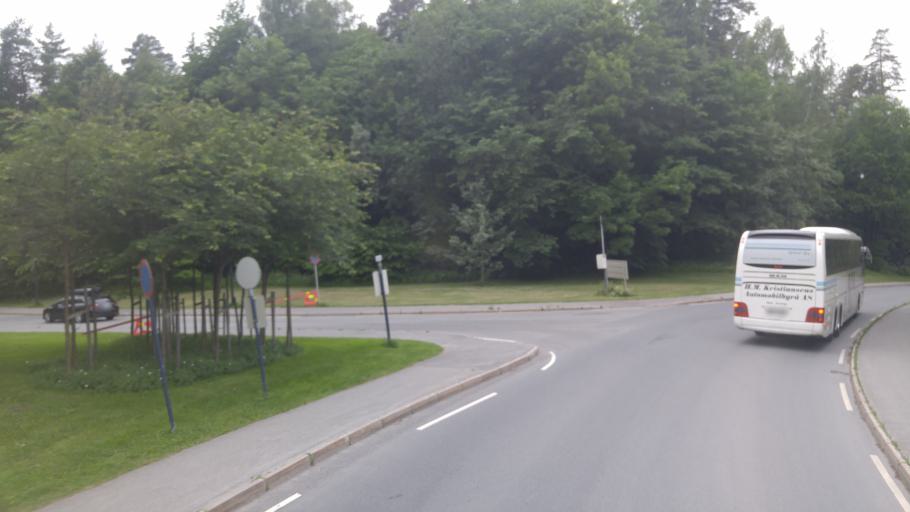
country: NO
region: Akershus
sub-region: Baerum
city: Sandvika
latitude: 59.8903
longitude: 10.5590
